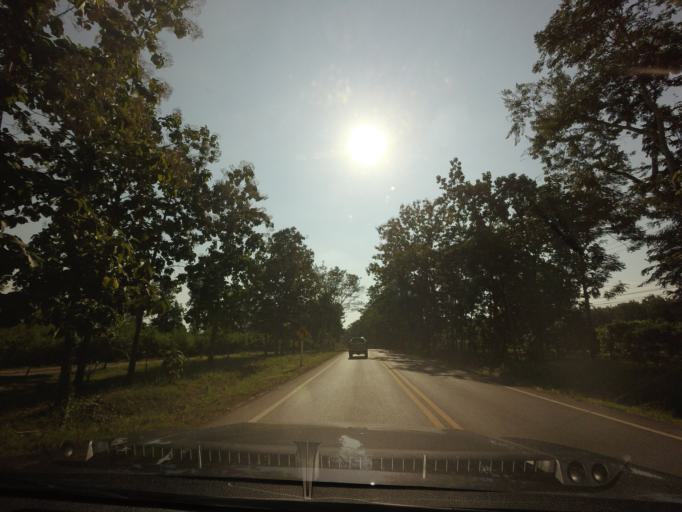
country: TH
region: Nan
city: Nan
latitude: 18.8140
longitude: 100.8067
